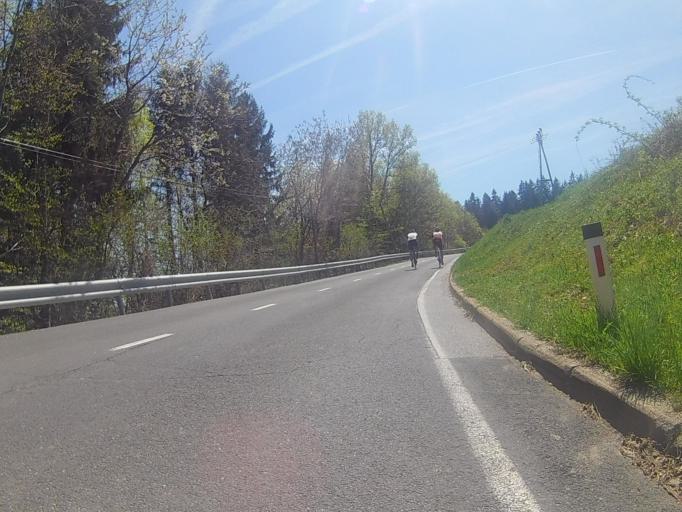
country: SI
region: Race-Fram
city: Fram
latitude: 46.4866
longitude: 15.5778
